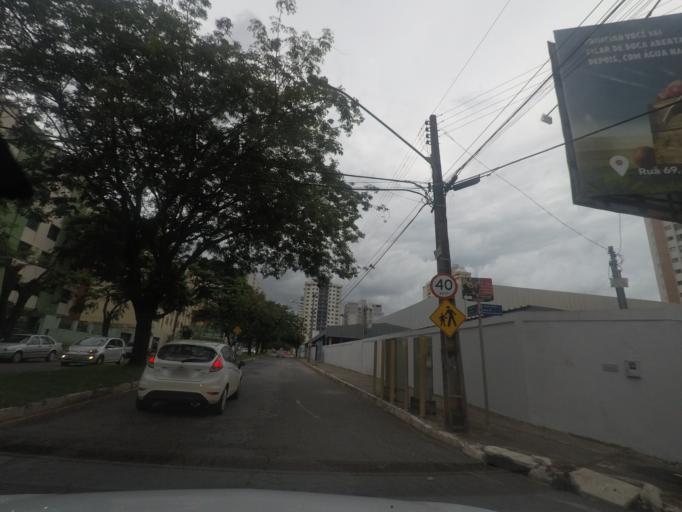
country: BR
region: Goias
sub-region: Goiania
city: Goiania
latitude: -16.6990
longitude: -49.2429
